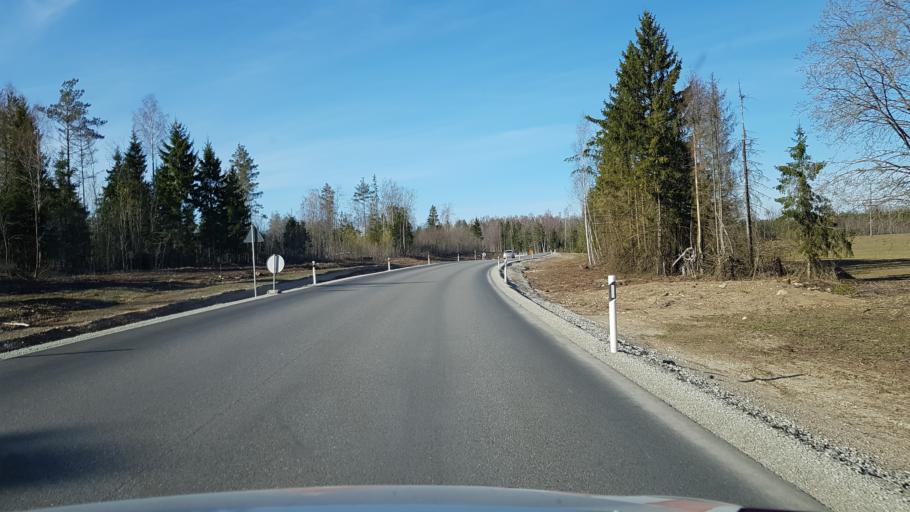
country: EE
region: Laeaene-Virumaa
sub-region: Vinni vald
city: Vinni
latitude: 59.1164
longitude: 26.6173
